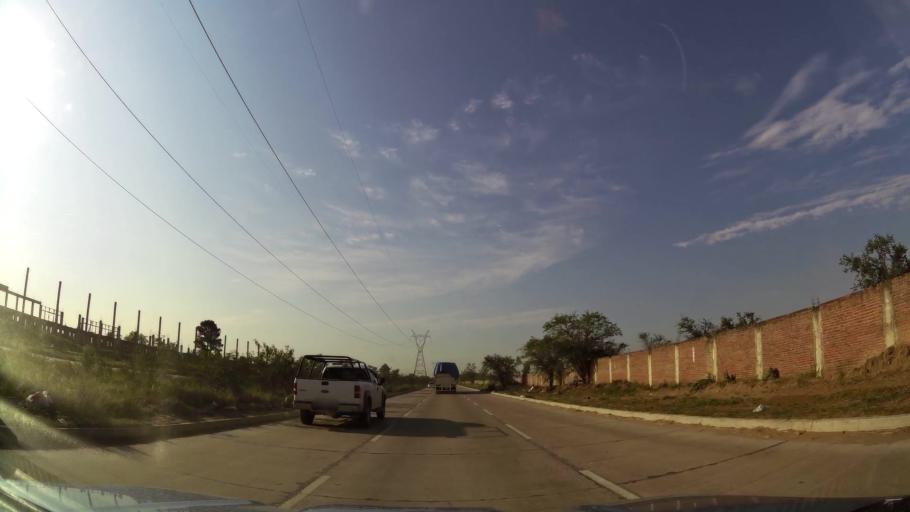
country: BO
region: Santa Cruz
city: Santa Cruz de la Sierra
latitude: -17.6918
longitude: -63.1414
